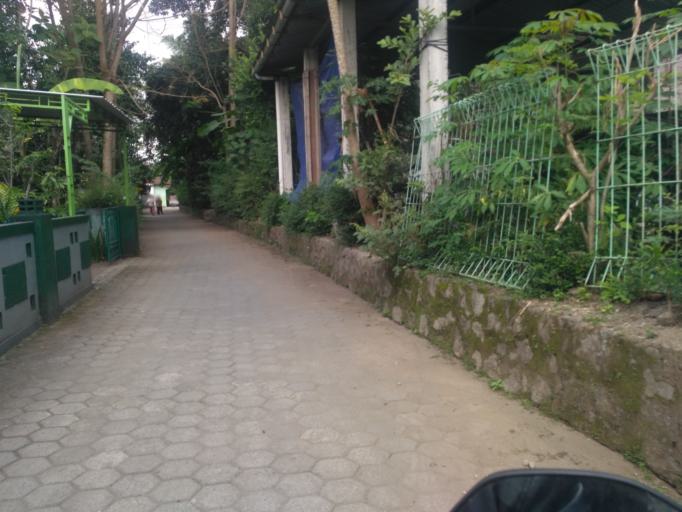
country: ID
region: Daerah Istimewa Yogyakarta
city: Melati
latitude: -7.7533
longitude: 110.3660
